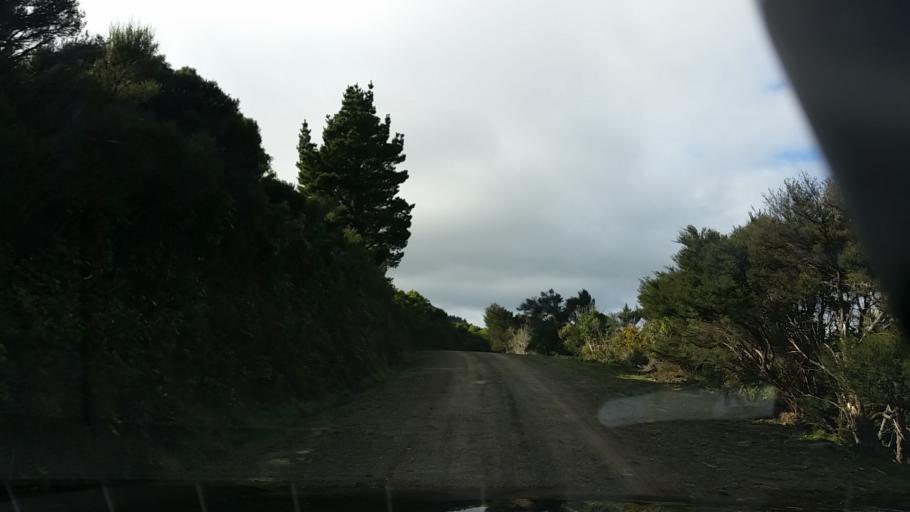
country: NZ
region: Marlborough
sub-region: Marlborough District
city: Picton
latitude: -40.9661
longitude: 173.8982
